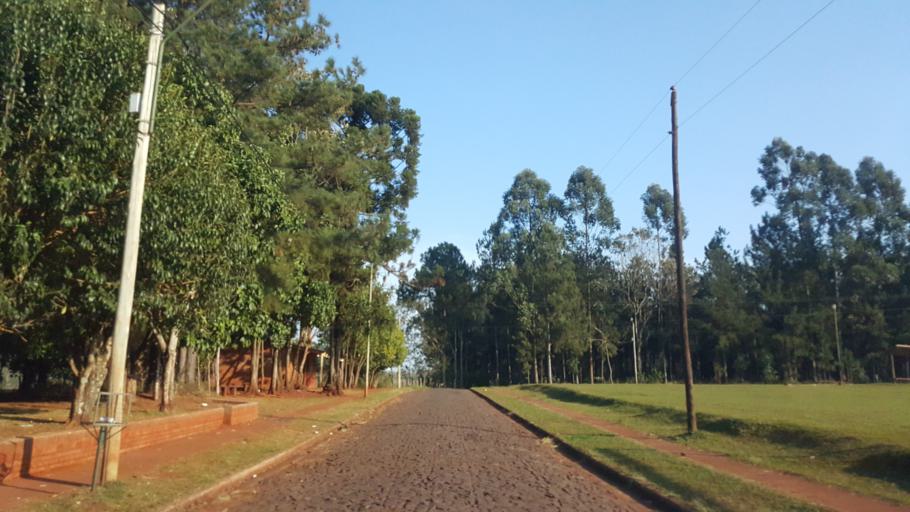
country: AR
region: Misiones
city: Capiovi
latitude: -26.8895
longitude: -55.0708
